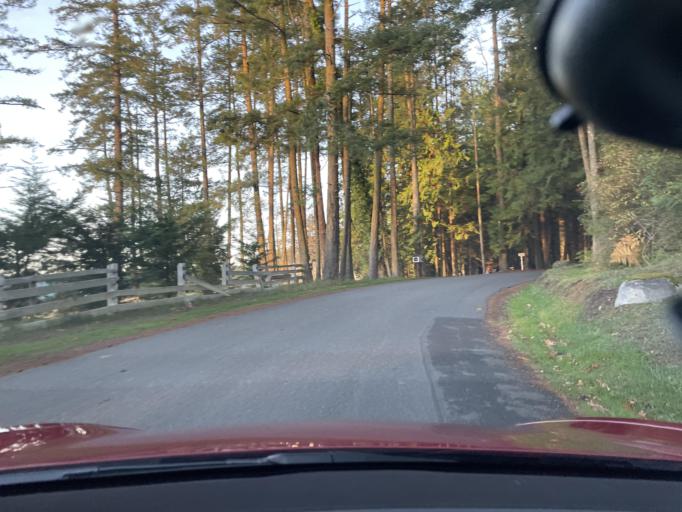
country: US
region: Washington
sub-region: San Juan County
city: Friday Harbor
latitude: 48.6144
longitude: -123.1543
